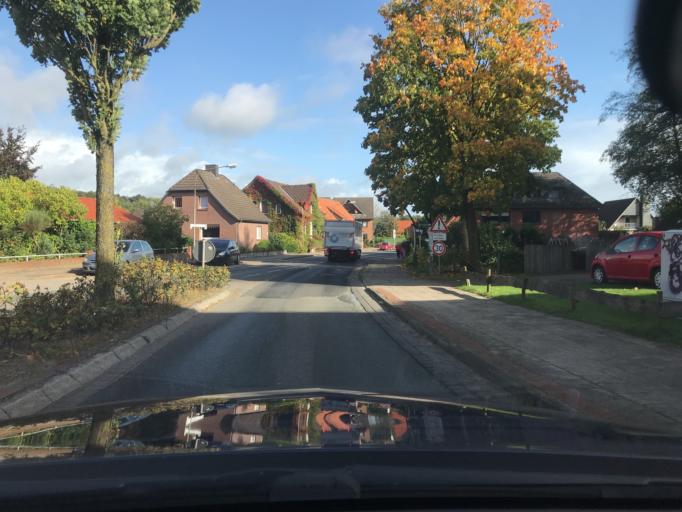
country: DE
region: Lower Saxony
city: Harsefeld
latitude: 53.4566
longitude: 9.4993
